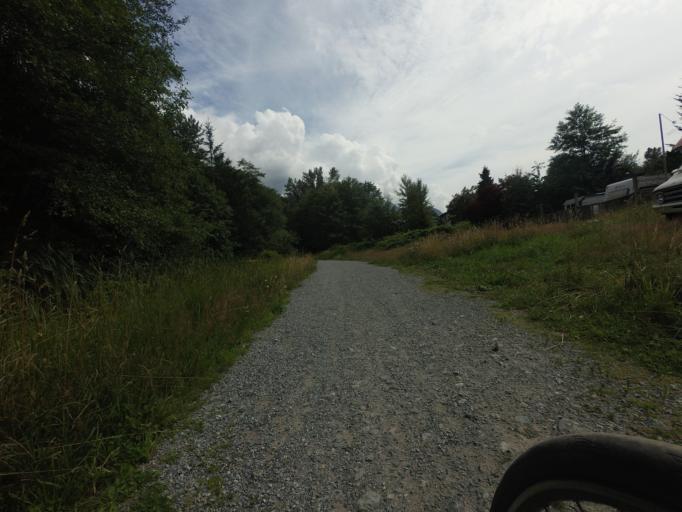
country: CA
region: British Columbia
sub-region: Greater Vancouver Regional District
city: Lions Bay
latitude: 49.7108
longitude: -123.1526
